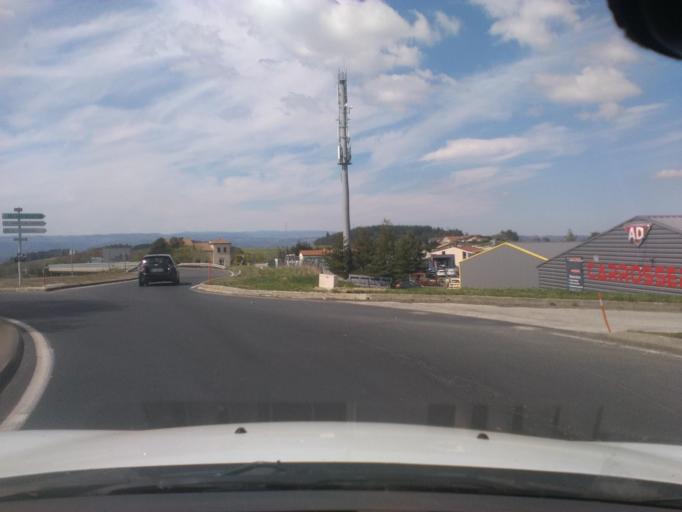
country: FR
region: Auvergne
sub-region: Departement de la Haute-Loire
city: La Seauve-sur-Semene
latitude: 45.3135
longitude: 4.2322
